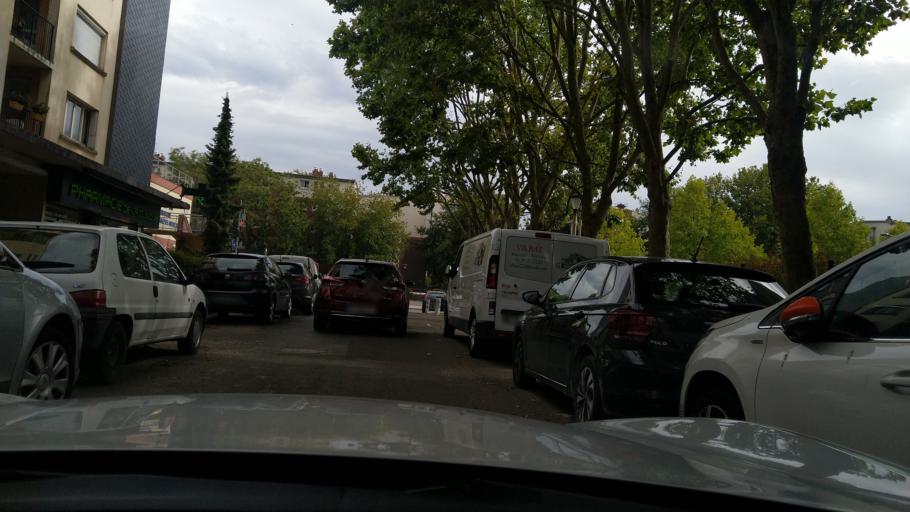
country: FR
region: Ile-de-France
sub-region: Departement de l'Essonne
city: Bievres
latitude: 48.7843
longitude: 2.2316
